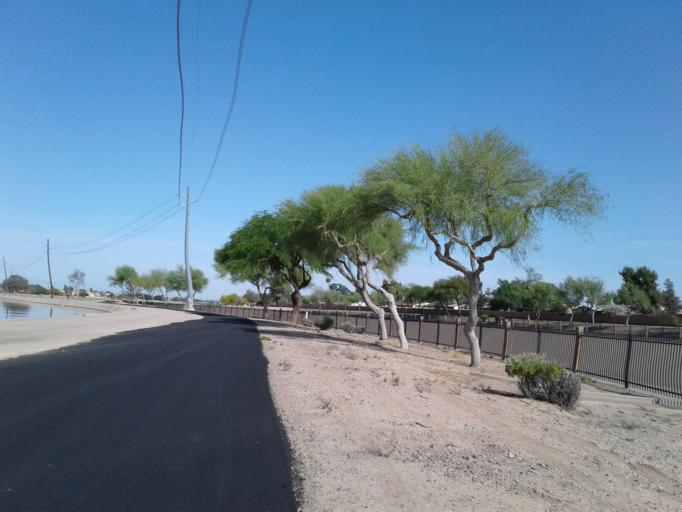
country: US
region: Arizona
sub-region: Maricopa County
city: Glendale
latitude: 33.5982
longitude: -112.1716
